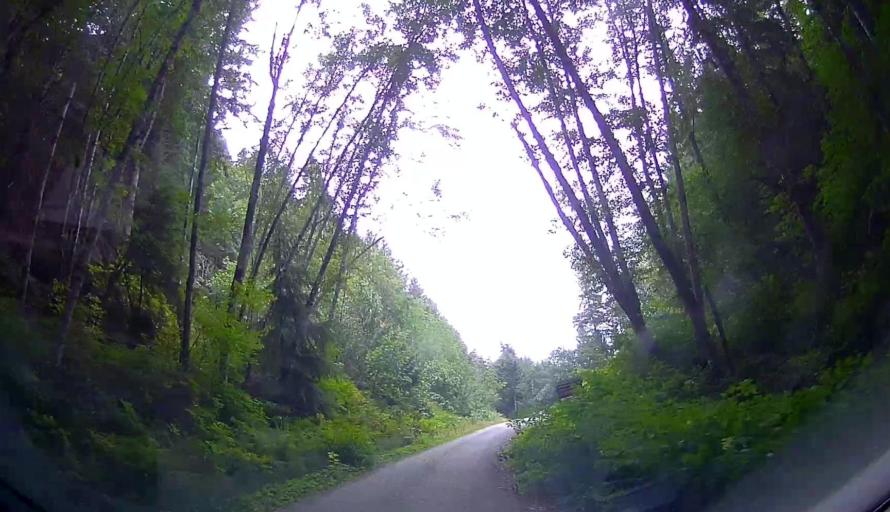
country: US
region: Washington
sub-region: Whatcom County
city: Sudden Valley
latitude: 48.6156
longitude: -122.3871
